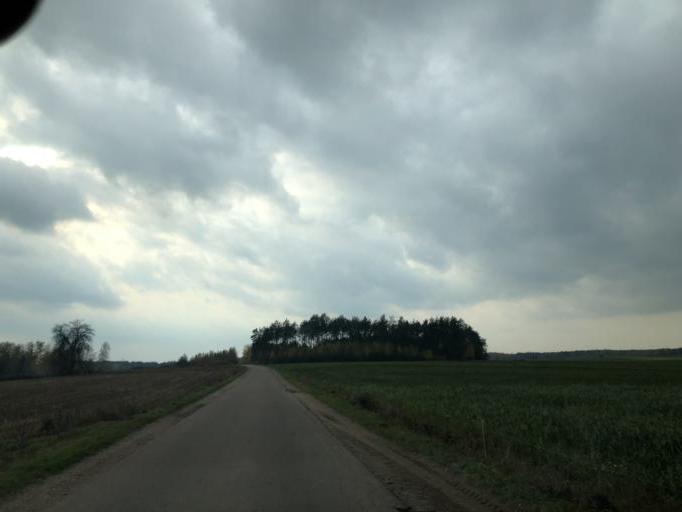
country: PL
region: Podlasie
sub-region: Lomza
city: Lomza
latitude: 53.1463
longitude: 21.9887
